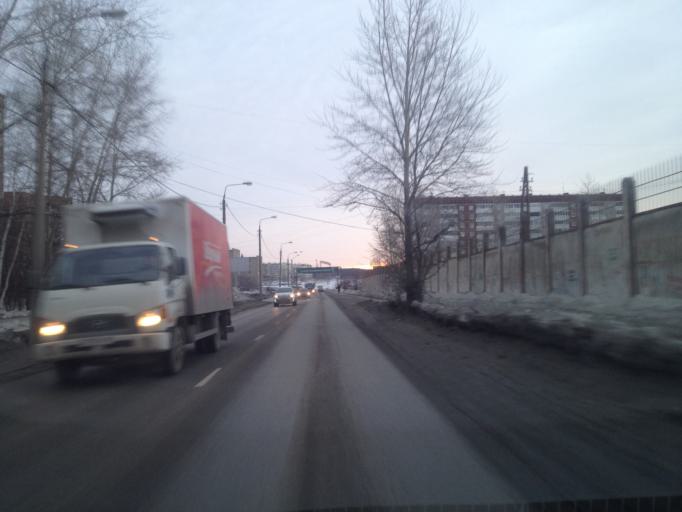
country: RU
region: Sverdlovsk
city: Sovkhoznyy
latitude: 56.7561
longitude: 60.6041
